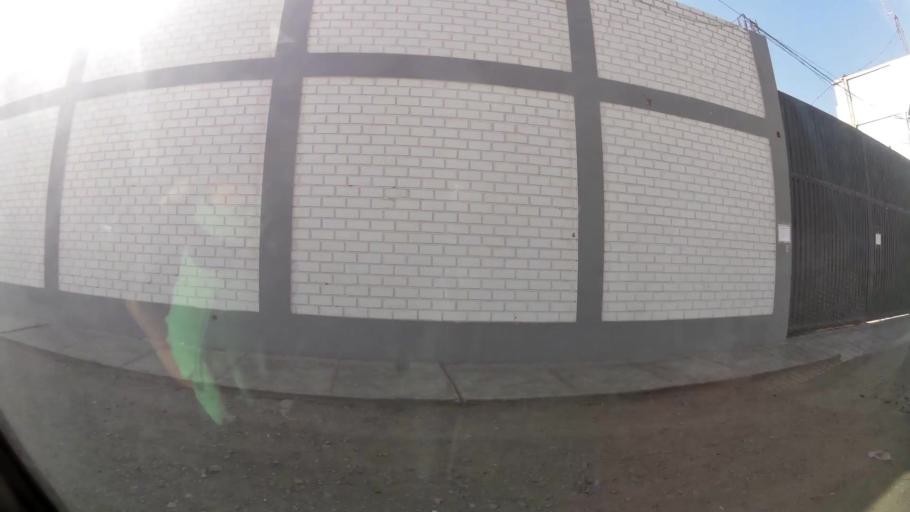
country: PE
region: Lima
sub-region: Huaura
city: Huacho
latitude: -11.1240
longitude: -77.6128
